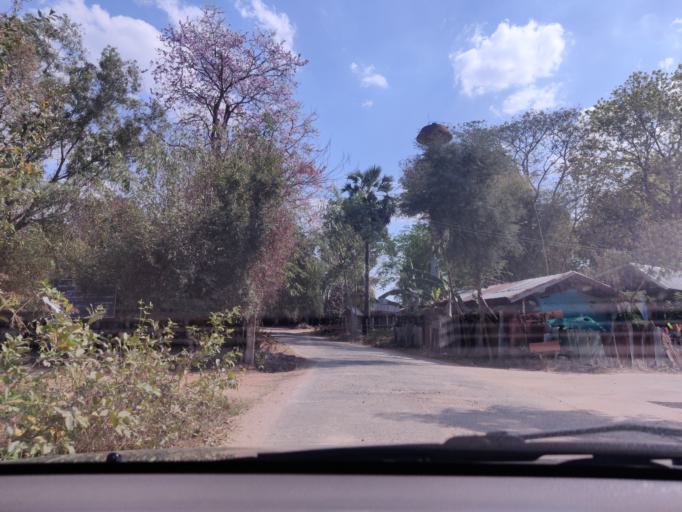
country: TH
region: Sisaket
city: Si Sa Ket
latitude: 15.0667
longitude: 104.3501
